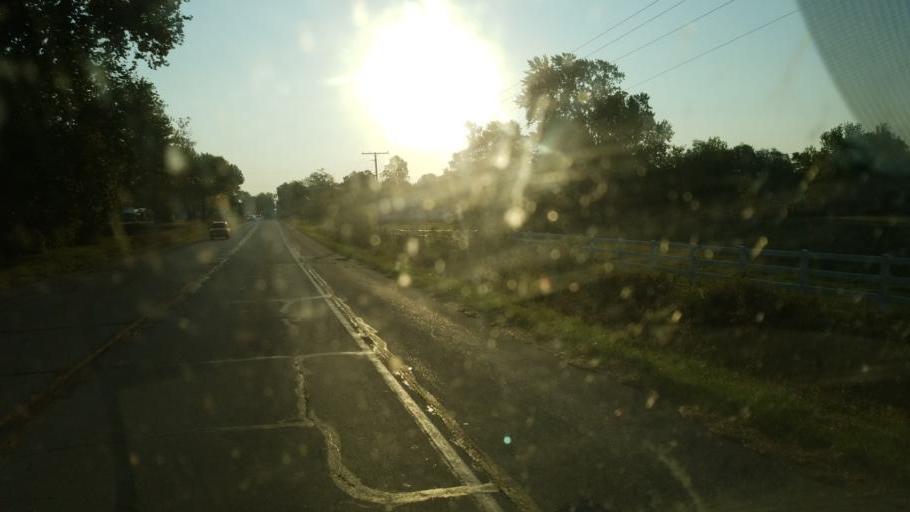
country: US
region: Indiana
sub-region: LaGrange County
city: Lagrange
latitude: 41.6413
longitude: -85.4330
